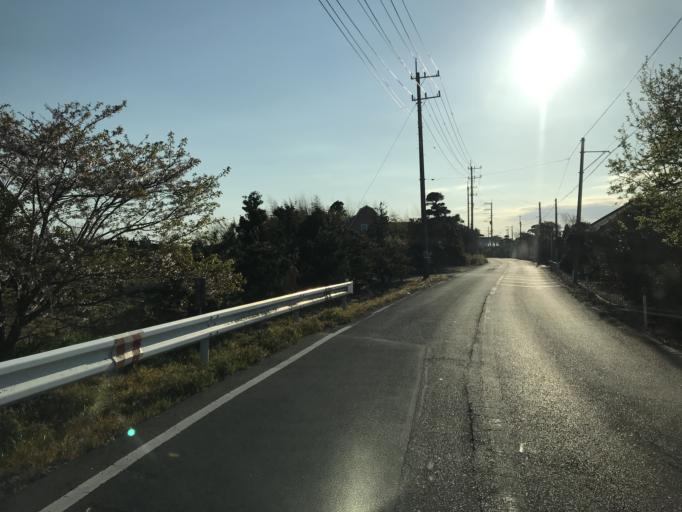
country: JP
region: Chiba
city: Asahi
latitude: 35.6823
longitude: 140.6053
